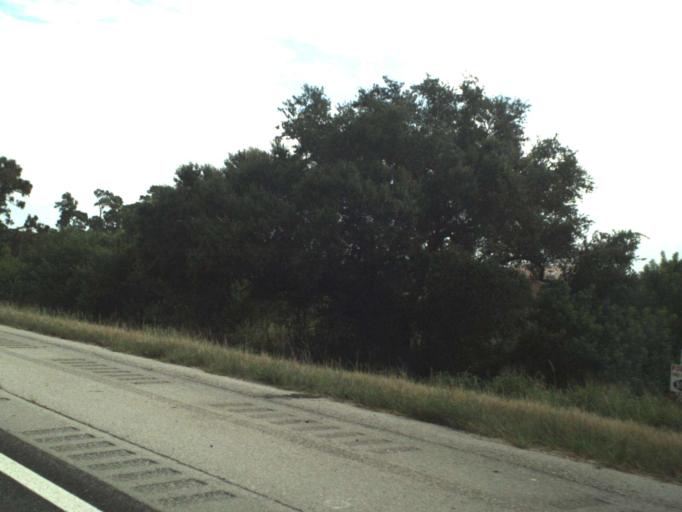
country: US
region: Florida
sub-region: Saint Lucie County
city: Fort Pierce South
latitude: 27.4034
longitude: -80.3883
